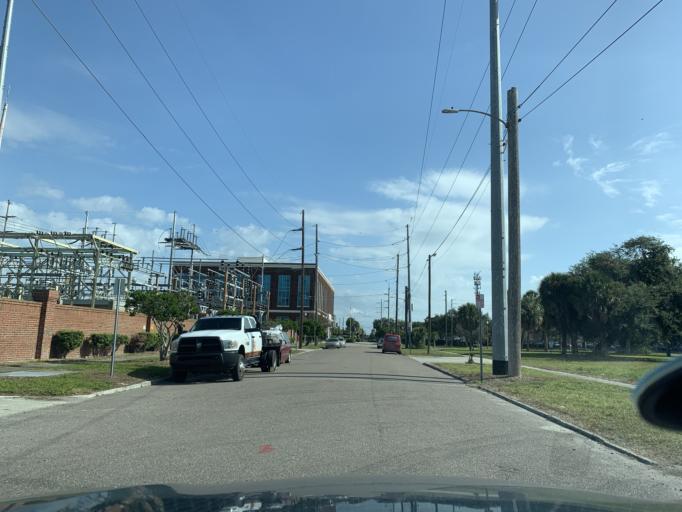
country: US
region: Florida
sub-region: Pinellas County
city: Saint Petersburg
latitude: 27.7578
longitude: -82.6382
